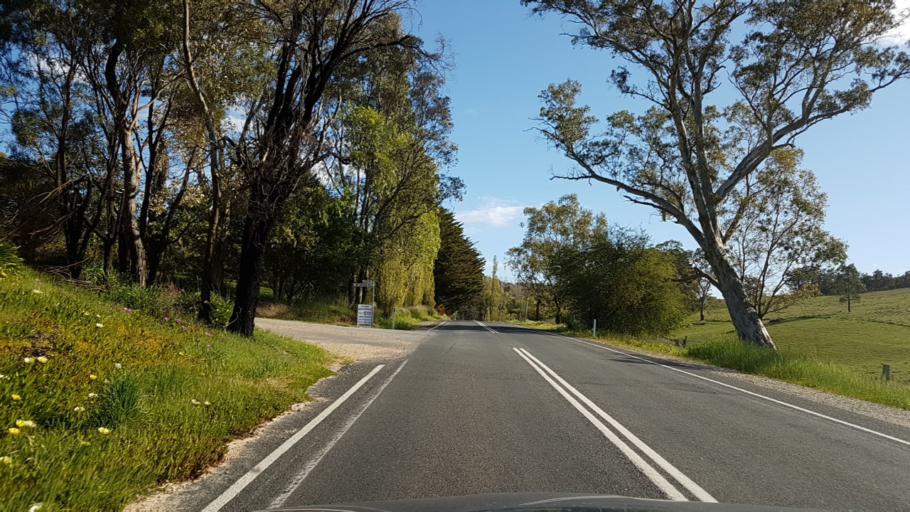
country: AU
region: South Australia
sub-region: Adelaide Hills
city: Gumeracha
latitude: -34.8644
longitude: 138.8897
